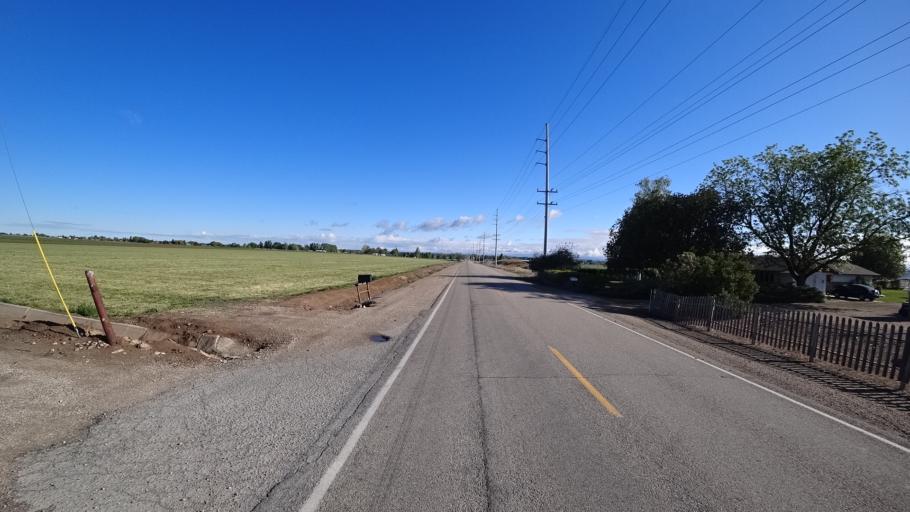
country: US
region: Idaho
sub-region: Ada County
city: Kuna
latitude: 43.4666
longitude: -116.4138
